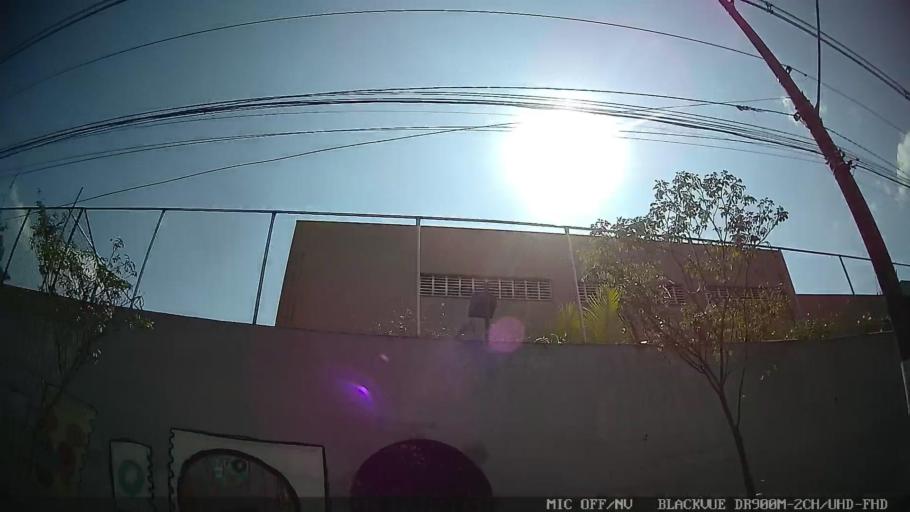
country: BR
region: Sao Paulo
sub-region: Guarulhos
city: Guarulhos
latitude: -23.4908
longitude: -46.4540
